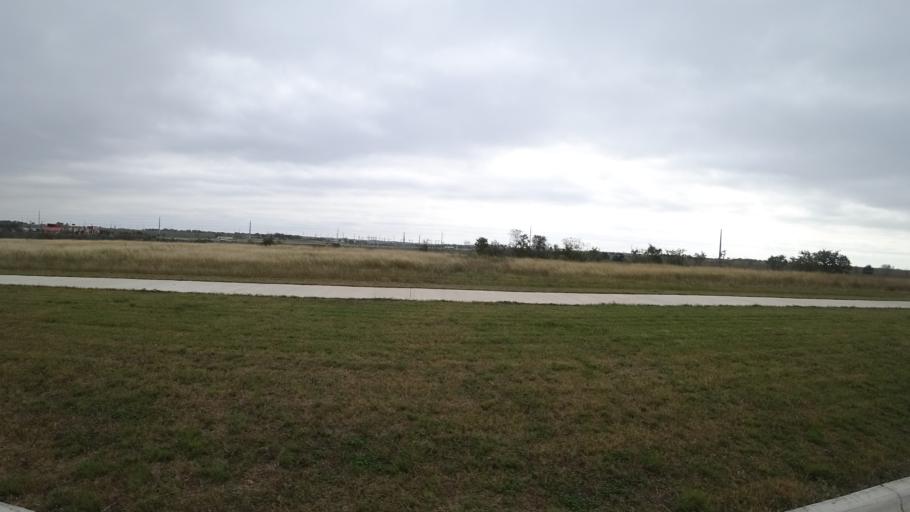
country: US
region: Texas
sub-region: Travis County
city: Pflugerville
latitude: 30.4121
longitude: -97.5907
